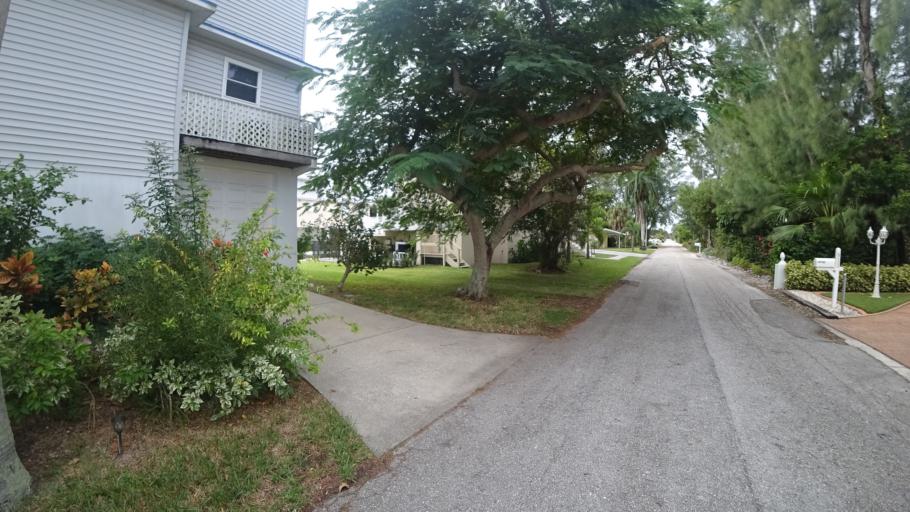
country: US
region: Florida
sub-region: Manatee County
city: Longboat Key
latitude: 27.4187
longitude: -82.6563
